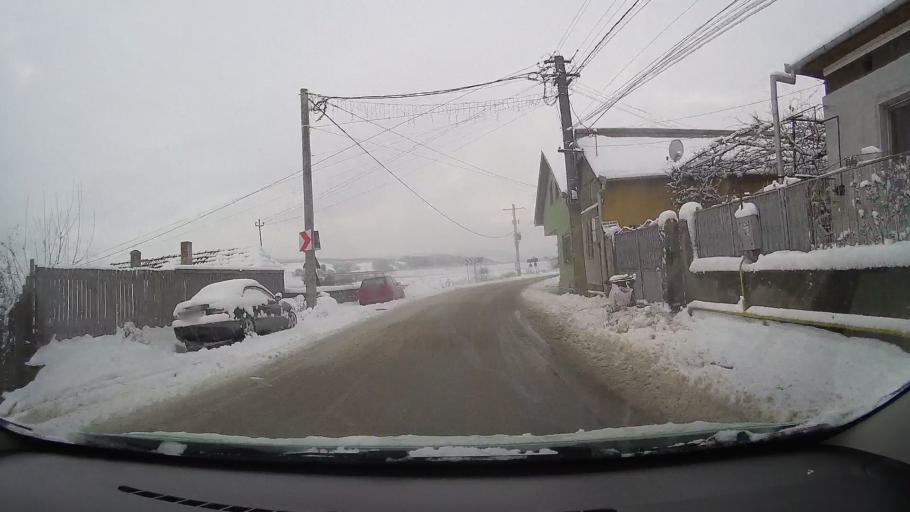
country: RO
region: Alba
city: Vurpar
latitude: 45.9736
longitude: 23.4809
